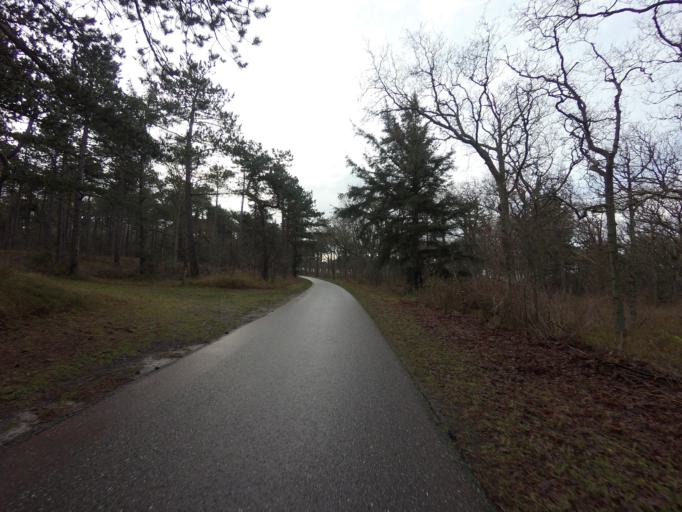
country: NL
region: North Holland
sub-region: Gemeente Texel
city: Den Burg
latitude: 53.0465
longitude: 4.7263
